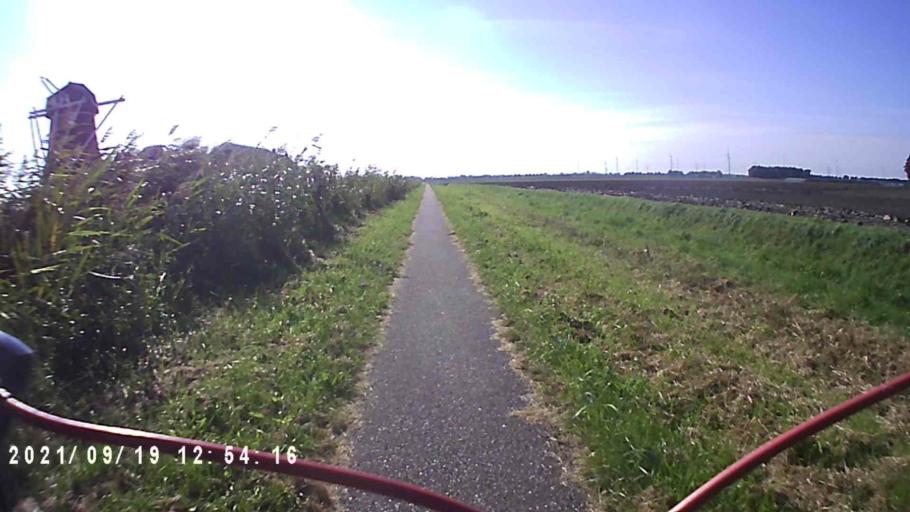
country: NL
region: Groningen
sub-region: Gemeente  Oldambt
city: Winschoten
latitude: 53.2000
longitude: 6.9486
